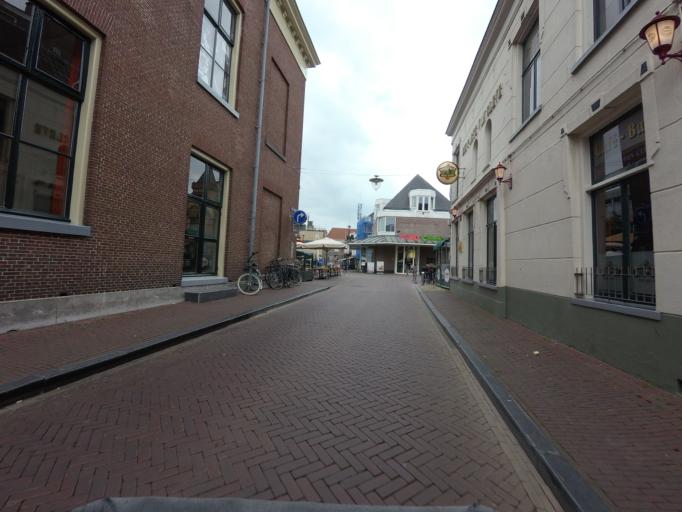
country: NL
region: Friesland
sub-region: Sudwest Fryslan
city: Sneek
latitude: 53.0326
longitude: 5.6599
